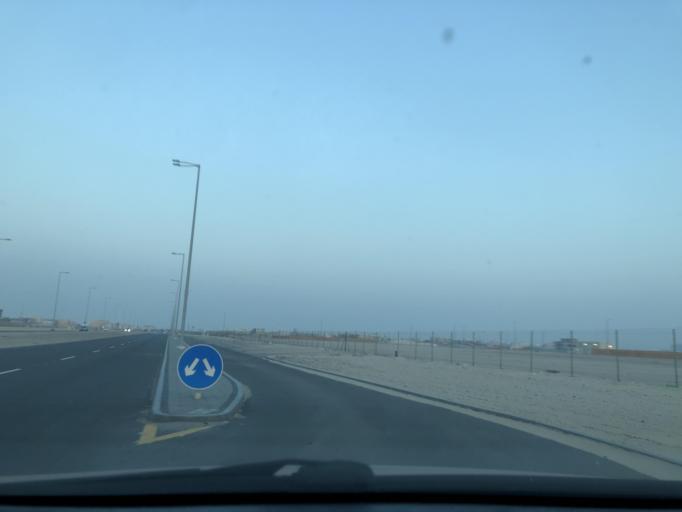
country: AE
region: Abu Dhabi
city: Abu Dhabi
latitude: 24.3609
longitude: 54.6056
